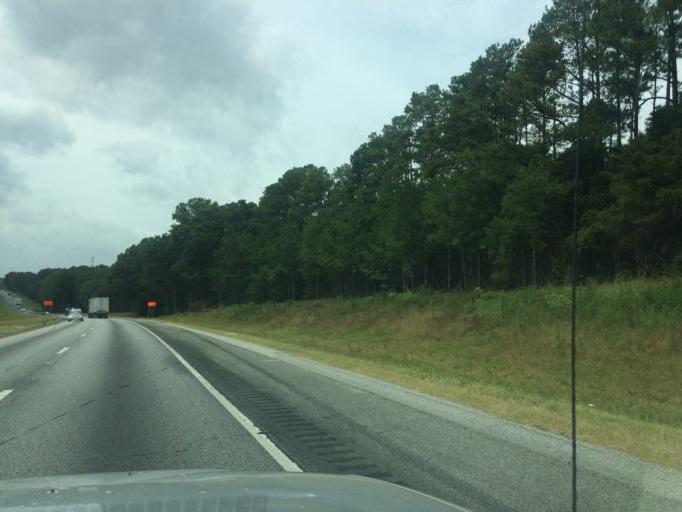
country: US
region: South Carolina
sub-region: Anderson County
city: Northlake
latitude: 34.5727
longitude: -82.7231
